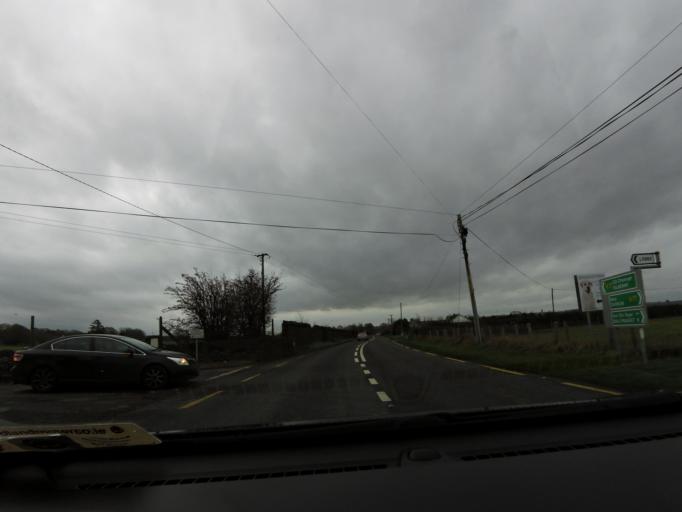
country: IE
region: Leinster
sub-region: Kilkenny
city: Ballyragget
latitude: 52.7427
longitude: -7.3211
